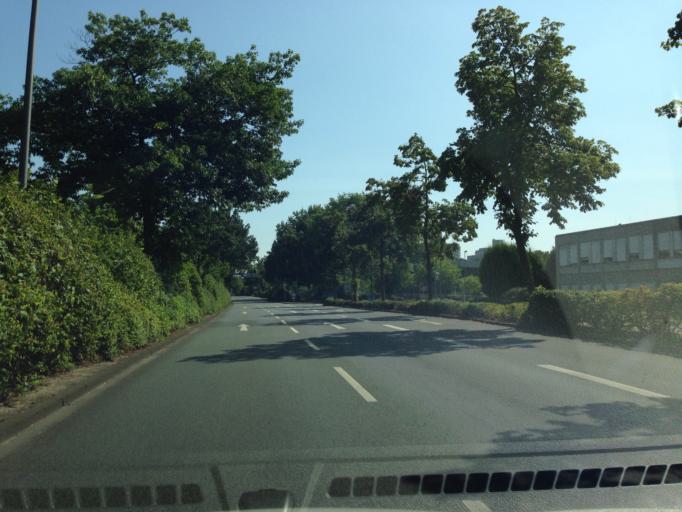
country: DE
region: North Rhine-Westphalia
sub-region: Regierungsbezirk Munster
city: Muenster
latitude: 51.9675
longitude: 7.6021
